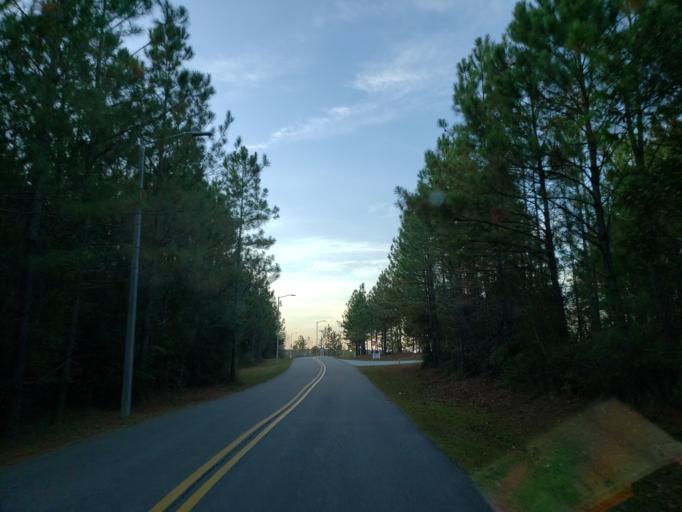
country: US
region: Mississippi
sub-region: Forrest County
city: Hattiesburg
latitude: 31.2788
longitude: -89.3116
